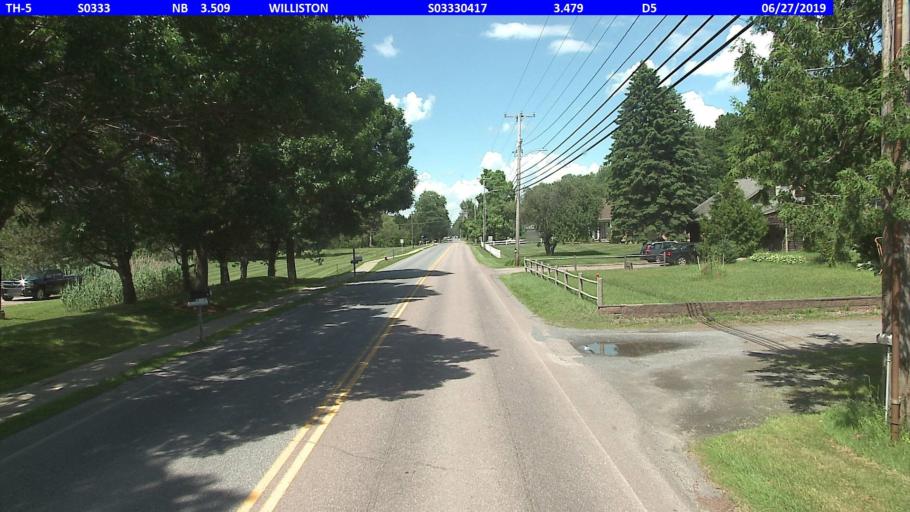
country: US
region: Vermont
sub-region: Chittenden County
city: Essex Junction
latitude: 44.4501
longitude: -73.1259
